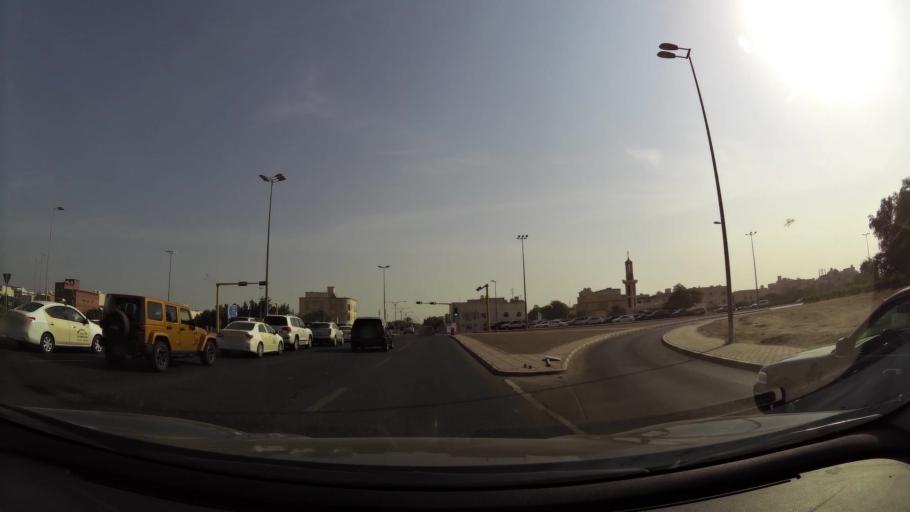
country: KW
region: Al Ahmadi
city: Ar Riqqah
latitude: 29.1600
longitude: 48.1028
